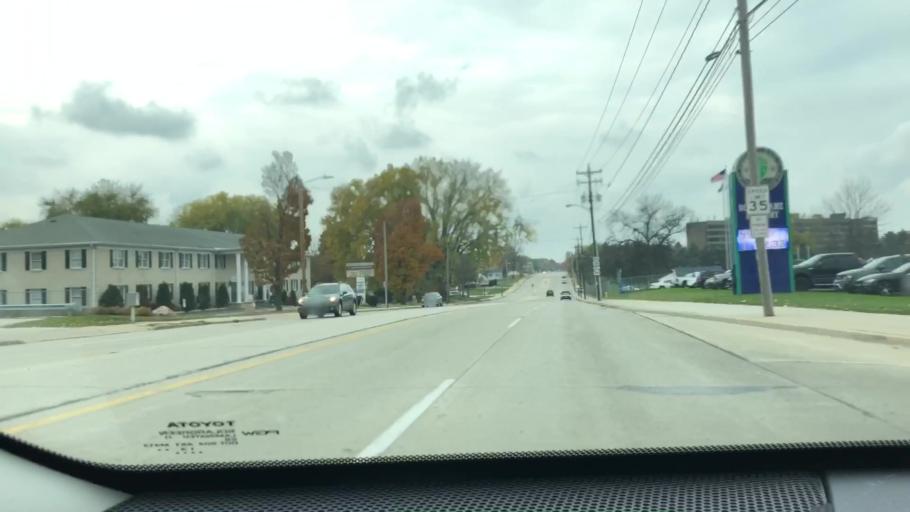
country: US
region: Wisconsin
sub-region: Brown County
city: Green Bay
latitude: 44.5200
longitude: -88.0533
